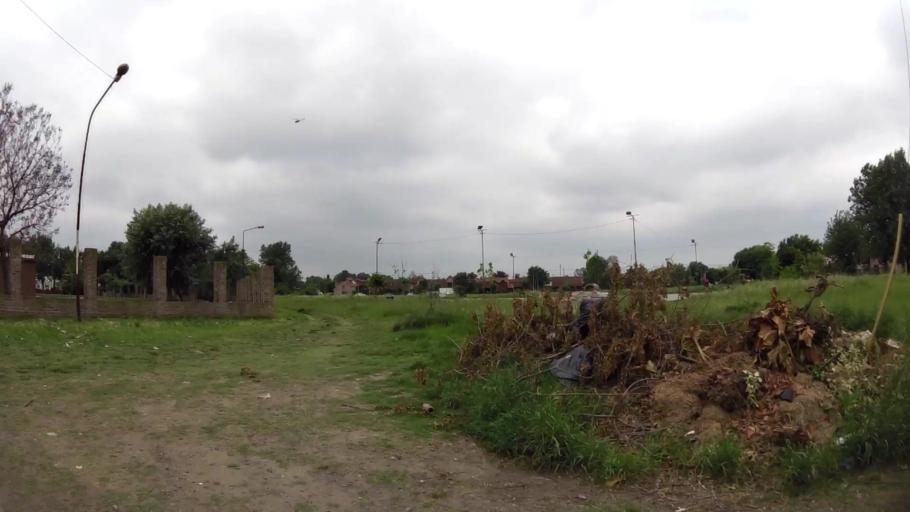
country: AR
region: Buenos Aires
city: San Justo
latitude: -34.7205
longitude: -58.5222
